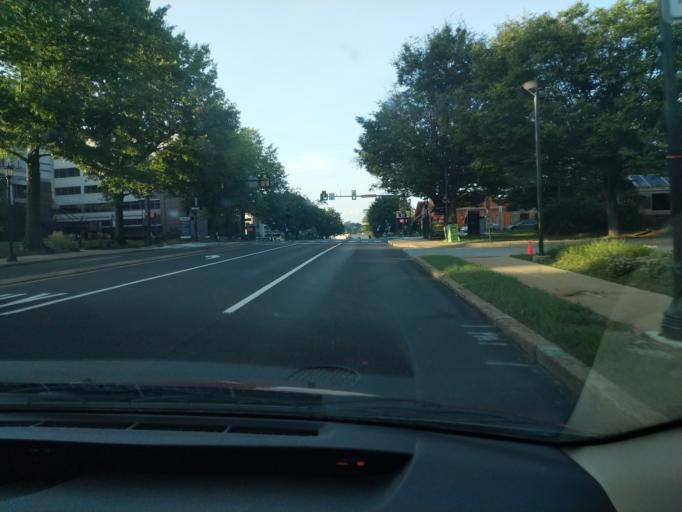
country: US
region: Pennsylvania
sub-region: Montgomery County
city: Jenkintown
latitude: 40.1185
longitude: -75.1196
